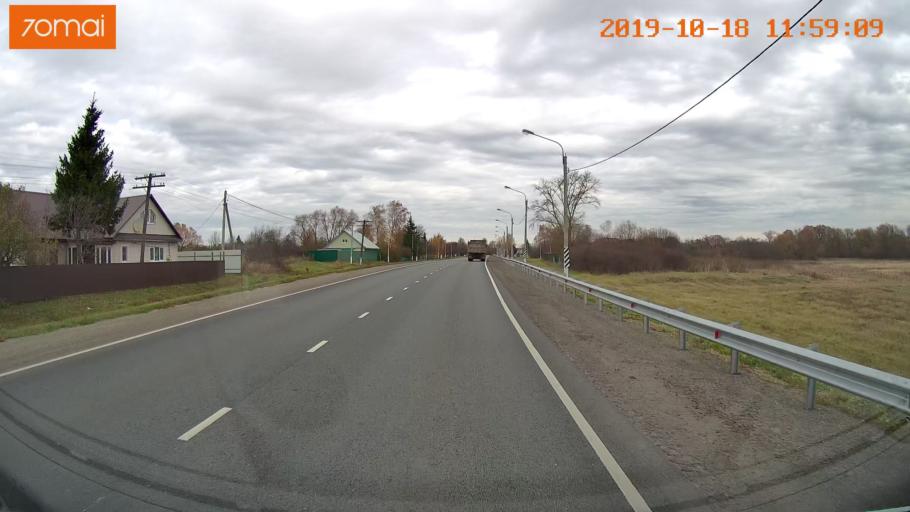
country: RU
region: Rjazan
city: Zakharovo
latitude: 54.2786
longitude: 39.1729
